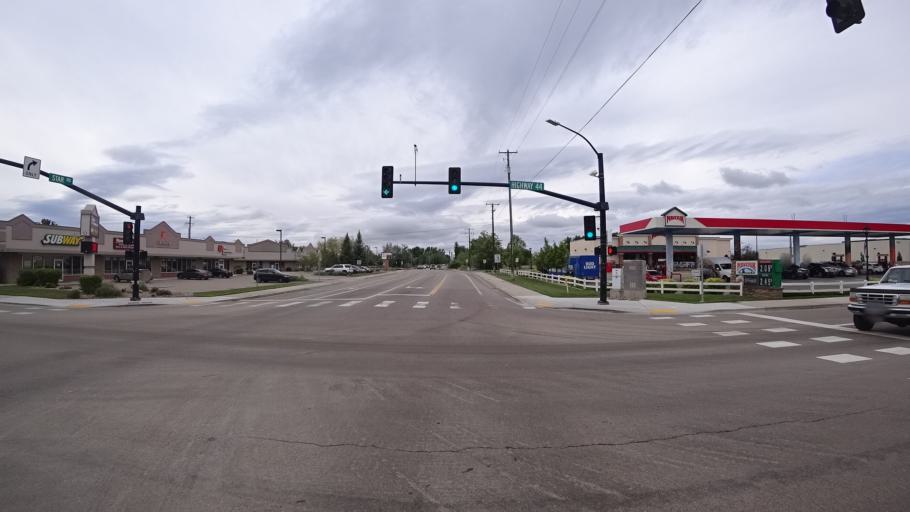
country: US
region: Idaho
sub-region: Ada County
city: Star
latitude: 43.6920
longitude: -116.4934
